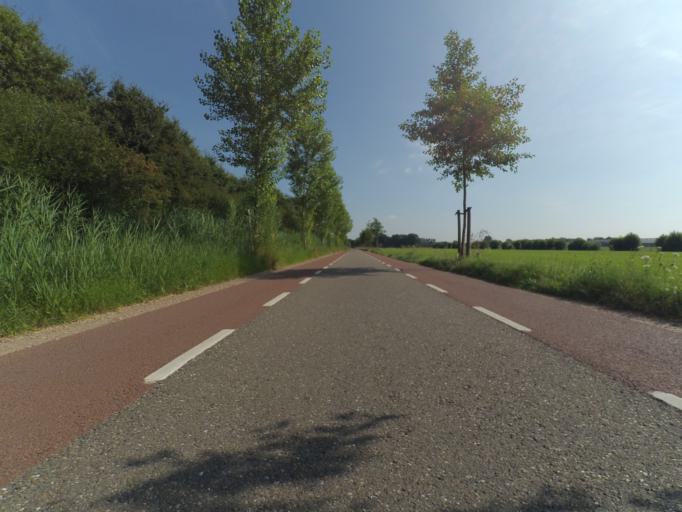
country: NL
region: Utrecht
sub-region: Gemeente Utrechtse Heuvelrug
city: Doorn
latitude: 52.0045
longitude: 5.3653
